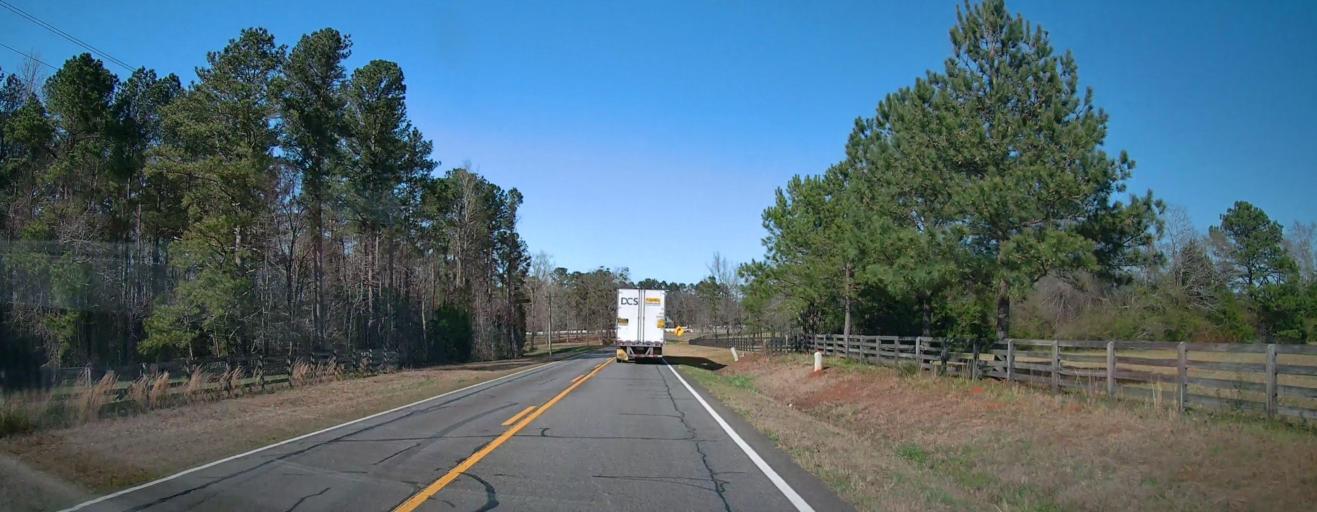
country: US
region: Georgia
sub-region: Butts County
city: Indian Springs
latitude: 33.1849
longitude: -83.9581
